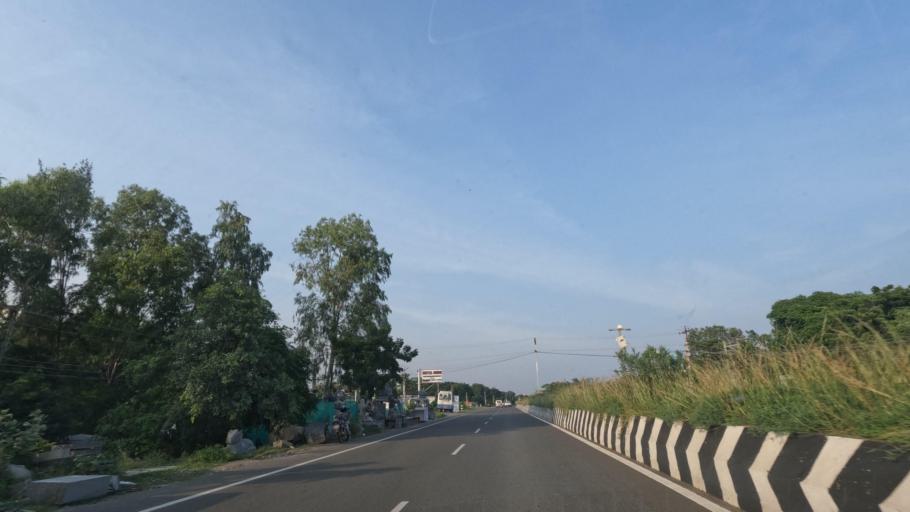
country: IN
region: Tamil Nadu
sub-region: Kancheepuram
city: Mamallapuram
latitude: 12.6422
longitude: 80.1998
